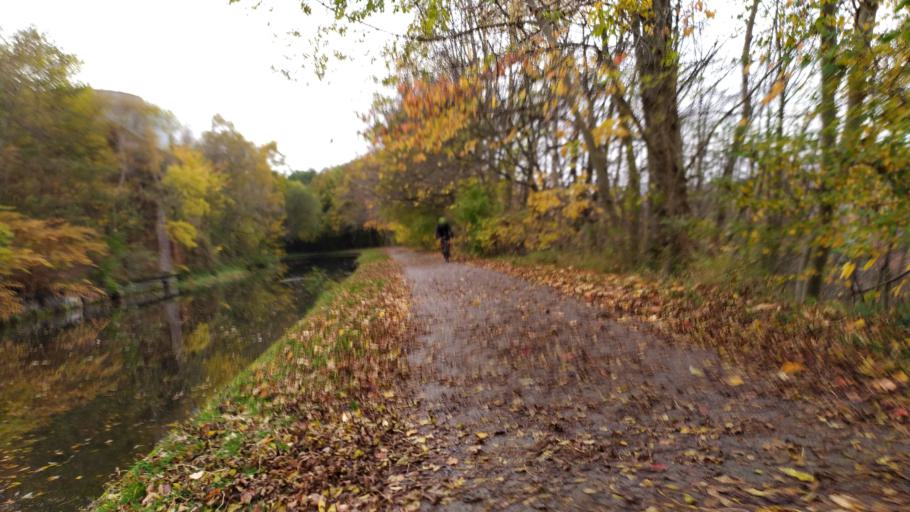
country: GB
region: England
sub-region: City and Borough of Leeds
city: Leeds
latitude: 53.8014
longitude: -1.5747
